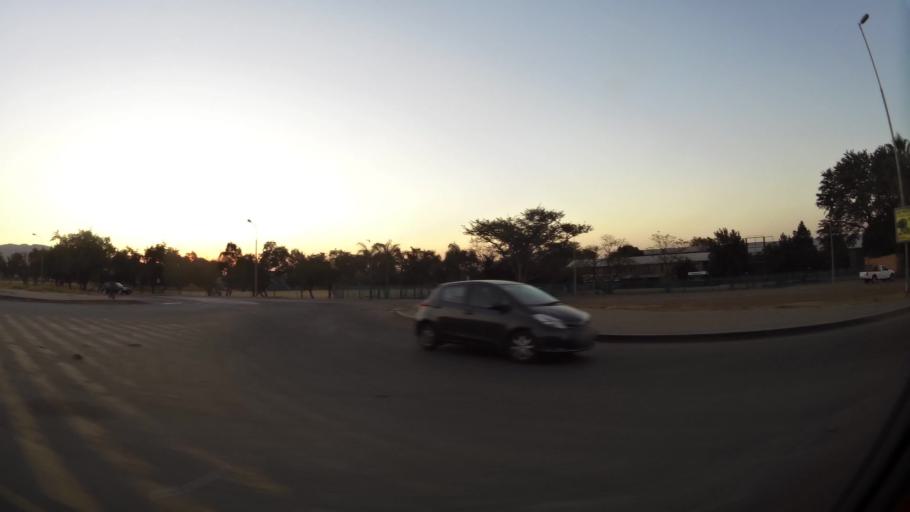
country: ZA
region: North-West
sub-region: Bojanala Platinum District Municipality
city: Rustenburg
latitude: -25.6542
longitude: 27.2457
